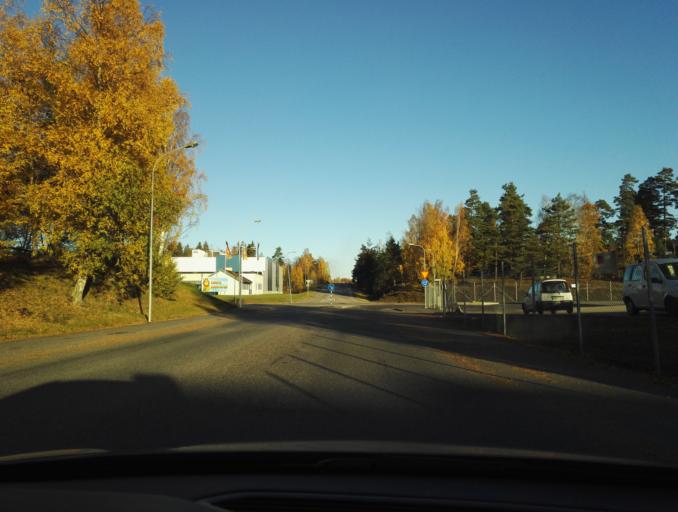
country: SE
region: Kronoberg
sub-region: Vaxjo Kommun
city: Vaexjoe
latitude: 56.8907
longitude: 14.7700
